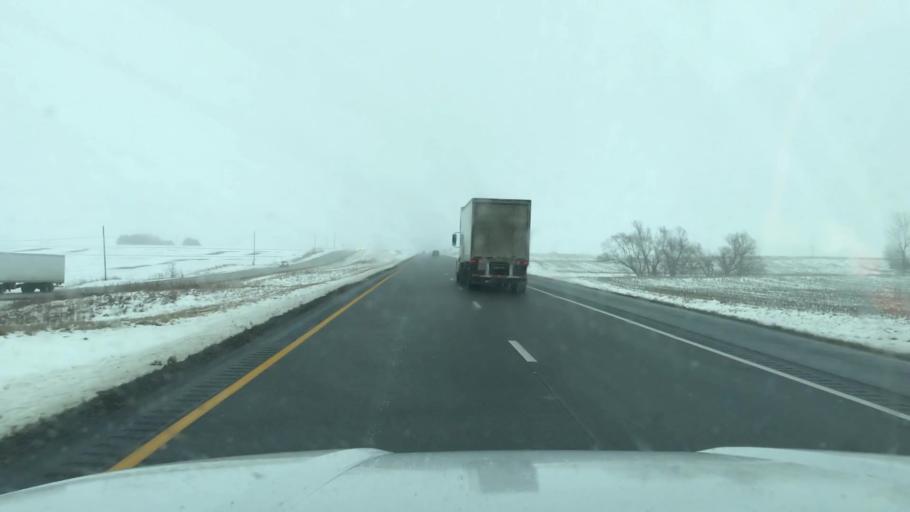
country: US
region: Missouri
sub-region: DeKalb County
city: Maysville
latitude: 39.7618
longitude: -94.4400
